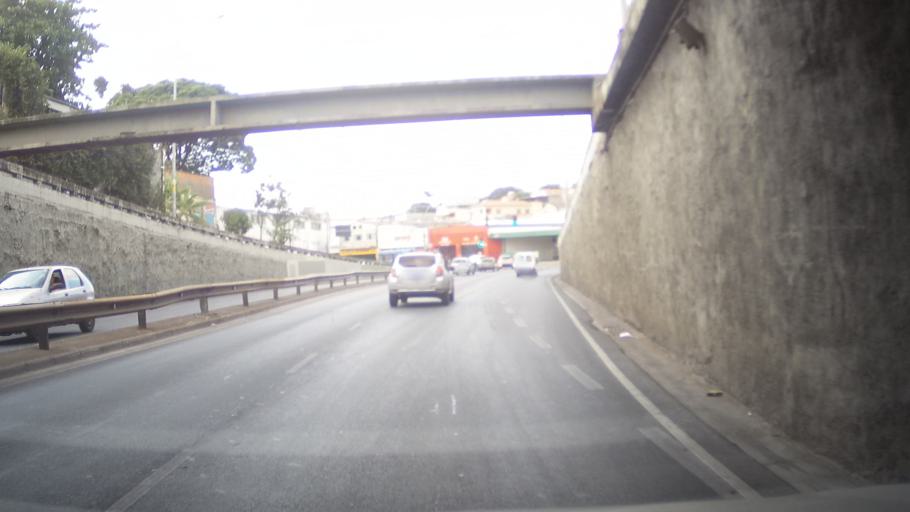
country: BR
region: Minas Gerais
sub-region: Belo Horizonte
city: Belo Horizonte
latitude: -19.9149
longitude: -43.9536
